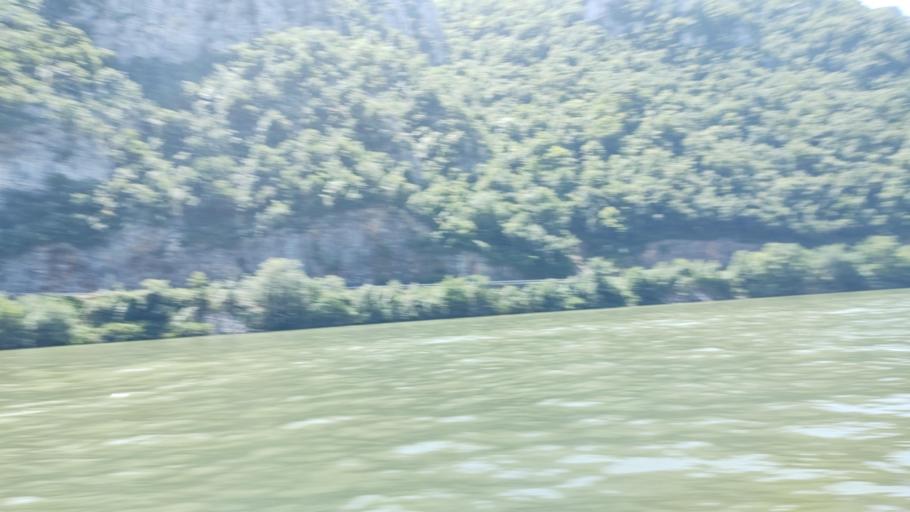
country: RO
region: Mehedinti
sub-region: Comuna Dubova
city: Dubova
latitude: 44.6303
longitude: 22.2851
